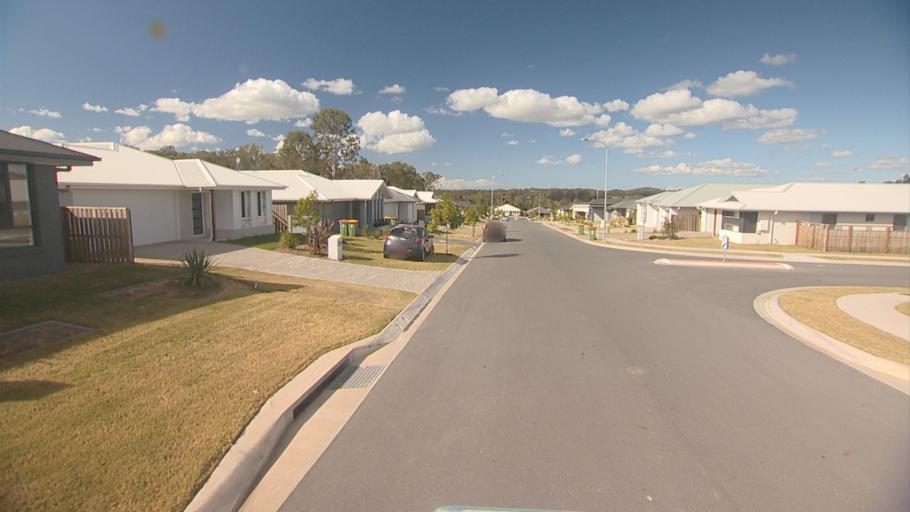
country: AU
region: Queensland
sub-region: Logan
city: Logan Reserve
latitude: -27.7130
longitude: 153.0853
